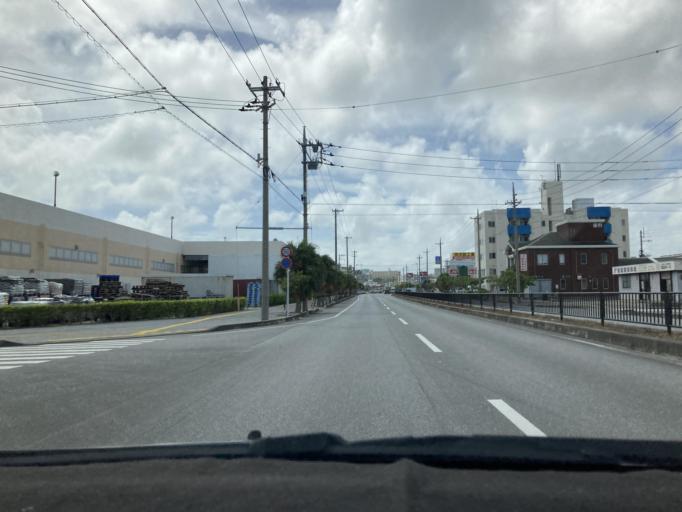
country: JP
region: Okinawa
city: Ginowan
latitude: 26.2075
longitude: 127.7632
